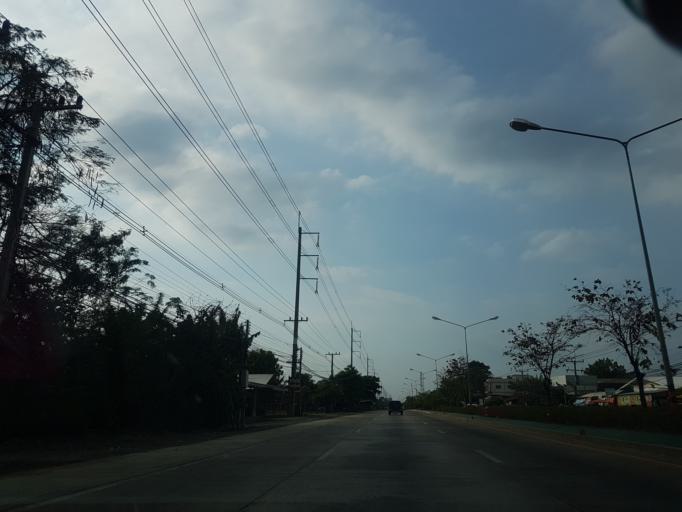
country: TH
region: Sara Buri
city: Phra Phutthabat
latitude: 14.7568
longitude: 100.7315
